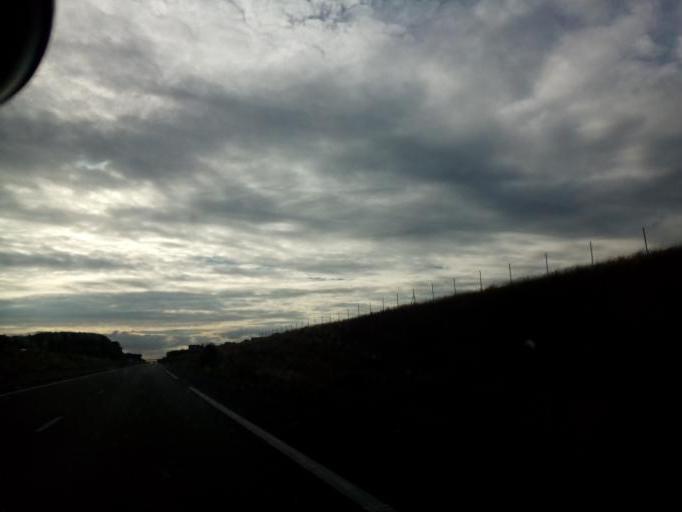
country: FR
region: Centre
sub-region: Departement d'Indre-et-Loire
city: Monts
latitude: 47.3066
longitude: 0.6336
